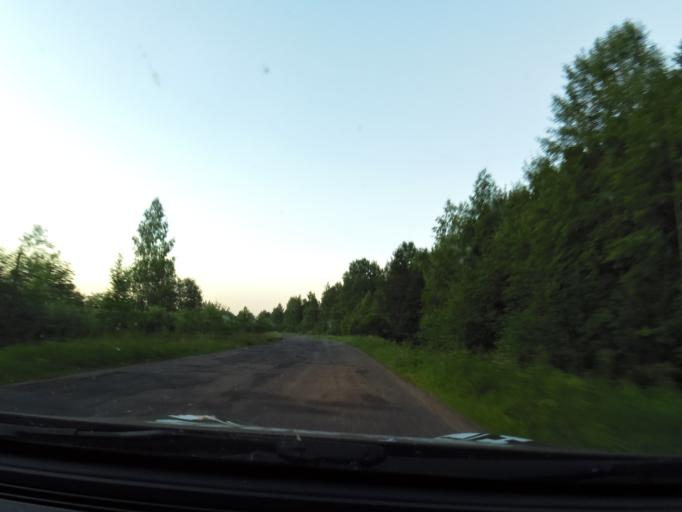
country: RU
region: Kostroma
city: Buy
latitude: 58.4417
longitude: 41.3437
